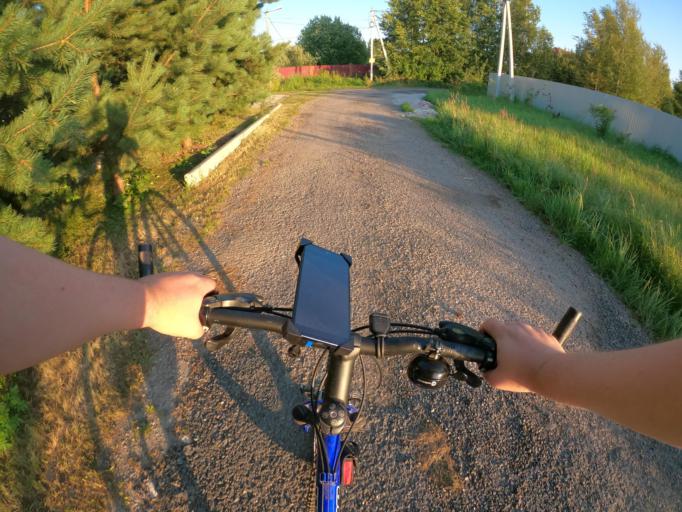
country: RU
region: Moskovskaya
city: Beloozerskiy
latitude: 55.4608
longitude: 38.4257
